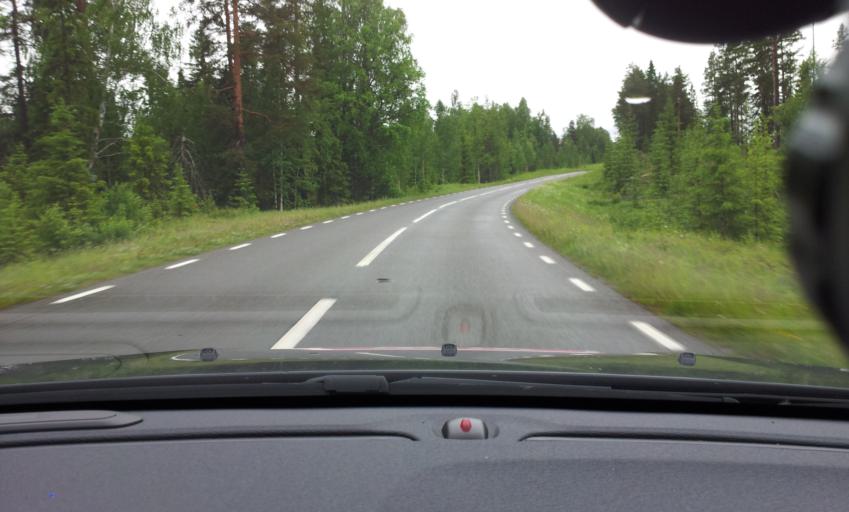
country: SE
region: Jaemtland
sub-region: Stroemsunds Kommun
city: Stroemsund
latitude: 63.4969
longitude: 15.4592
